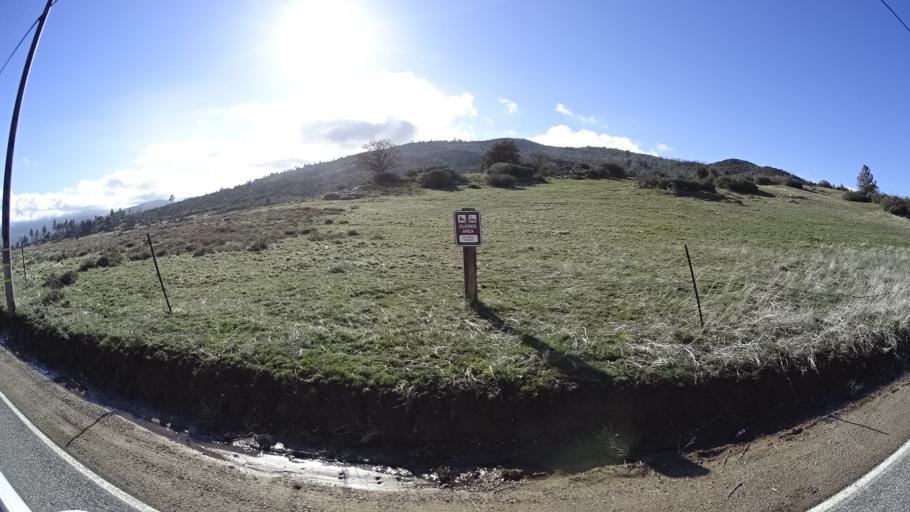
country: US
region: California
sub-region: San Diego County
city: Julian
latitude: 33.0050
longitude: -116.5643
